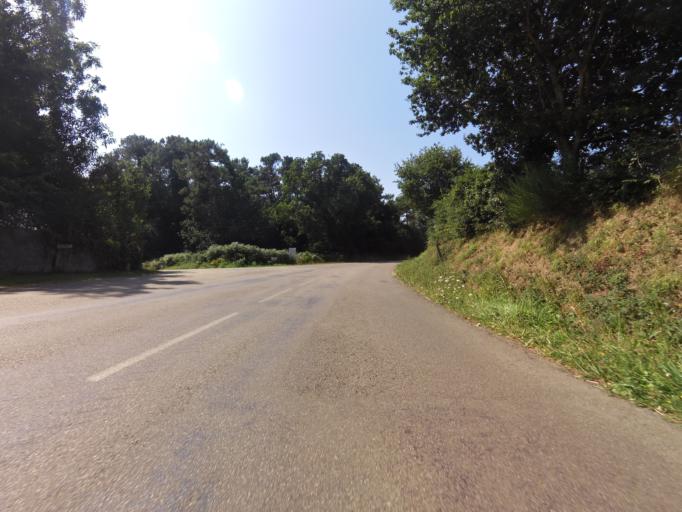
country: FR
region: Brittany
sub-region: Departement du Finistere
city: Ploneour-Lanvern
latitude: 47.9157
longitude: -4.3262
